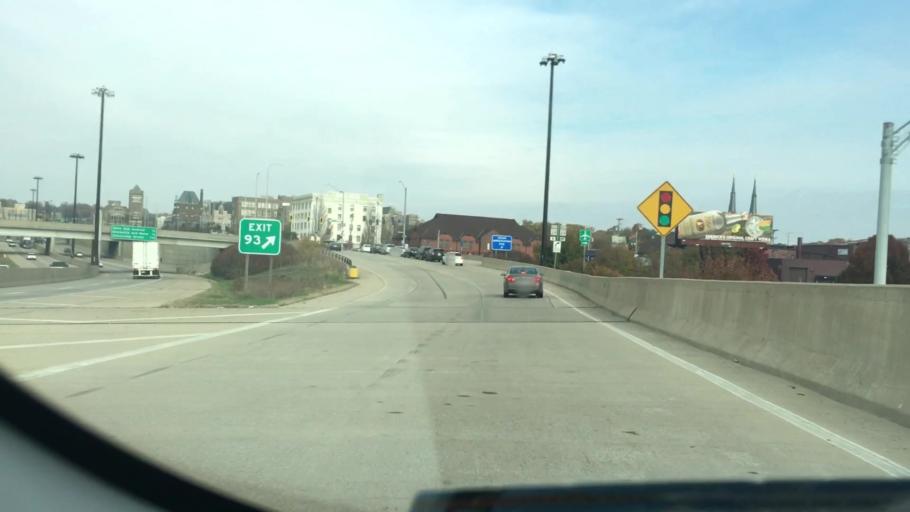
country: US
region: Illinois
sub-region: Peoria County
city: Peoria
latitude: 40.6927
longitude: -89.5852
